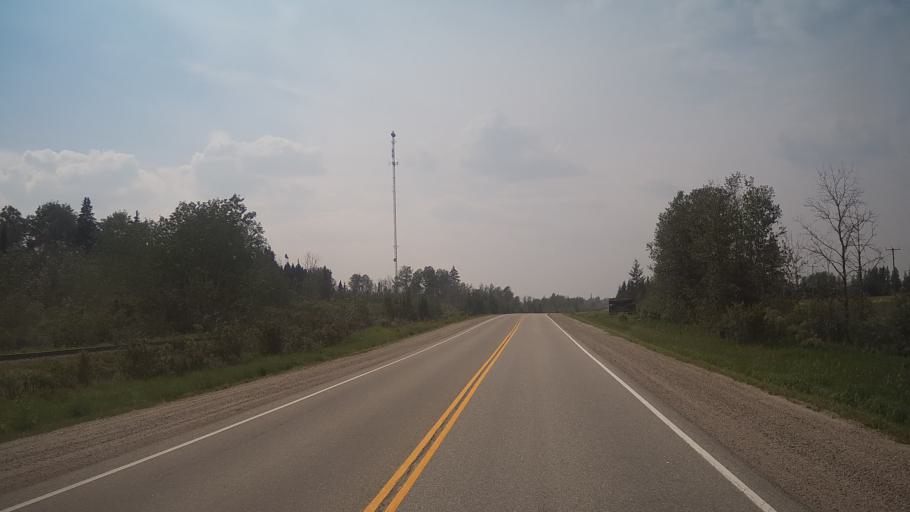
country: CA
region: Ontario
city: Kapuskasing
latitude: 49.3901
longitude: -82.3509
